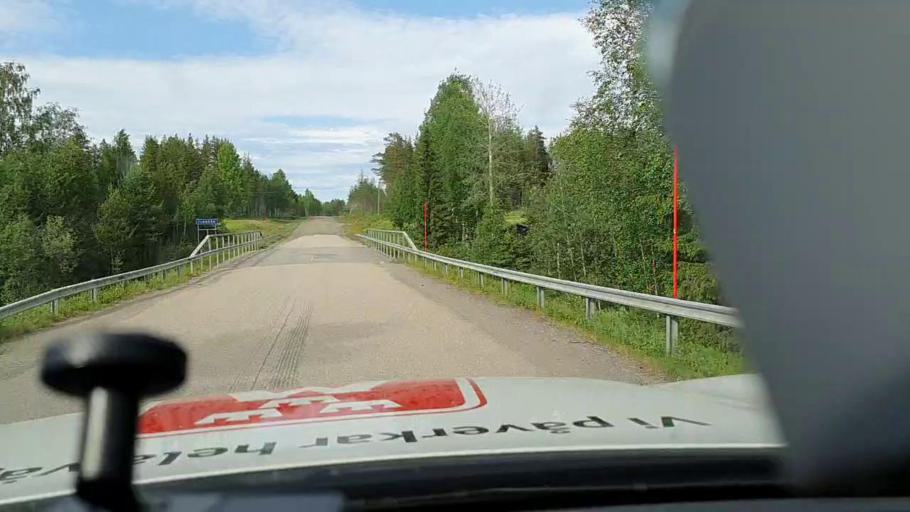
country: SE
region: Norrbotten
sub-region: Alvsbyns Kommun
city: AElvsbyn
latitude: 66.1499
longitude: 21.0308
